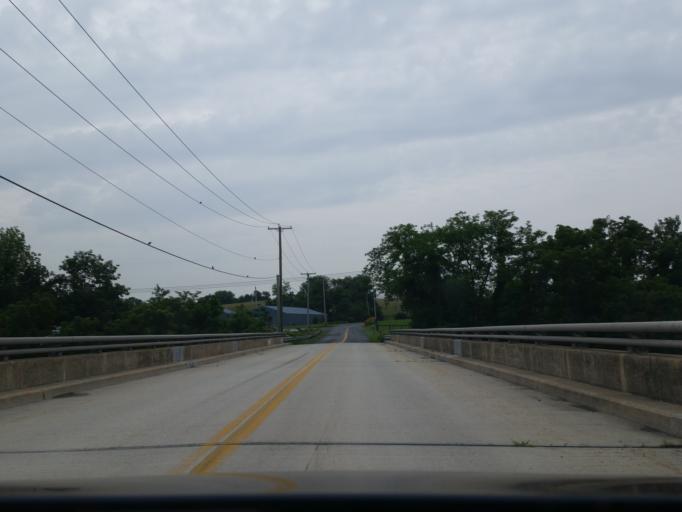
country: US
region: Pennsylvania
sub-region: Lebanon County
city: Palmyra
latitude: 40.3902
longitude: -76.6391
